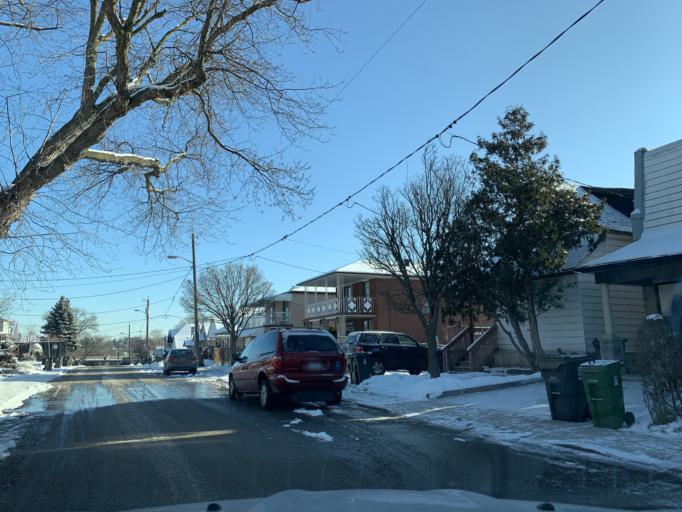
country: CA
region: Ontario
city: Toronto
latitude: 43.6829
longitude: -79.4856
